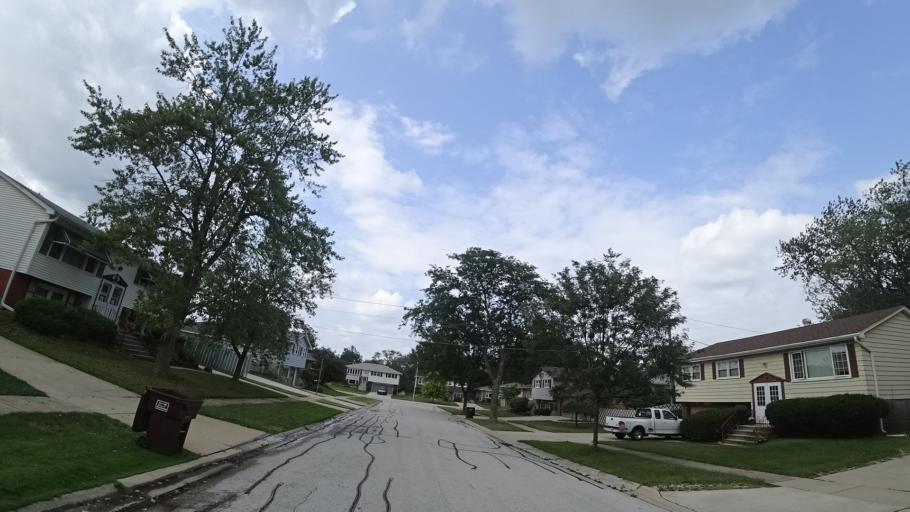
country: US
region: Illinois
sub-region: Cook County
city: Tinley Park
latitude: 41.5942
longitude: -87.7798
